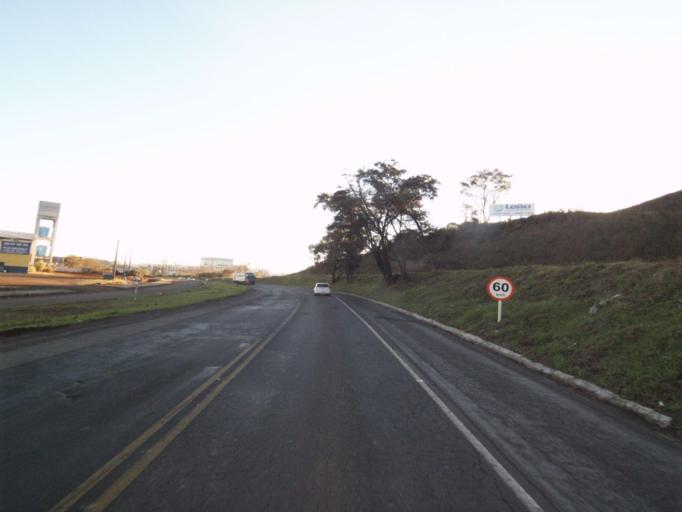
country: BR
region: Santa Catarina
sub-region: Chapeco
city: Chapeco
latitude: -26.8264
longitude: -53.0070
